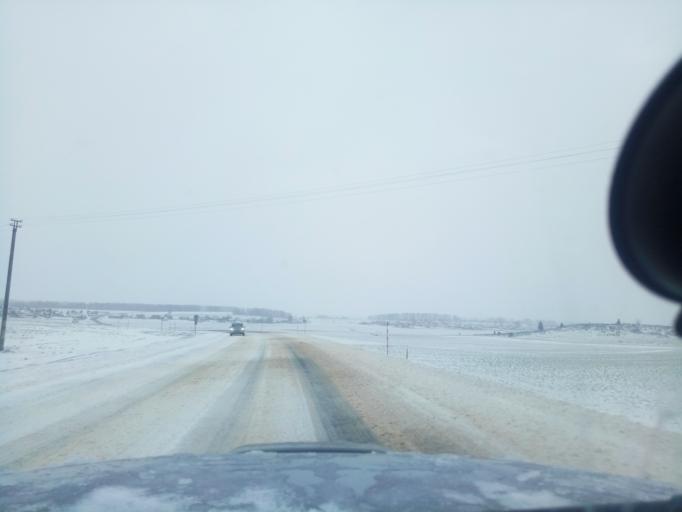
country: BY
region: Minsk
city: Haradzyeya
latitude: 53.3330
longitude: 26.5270
